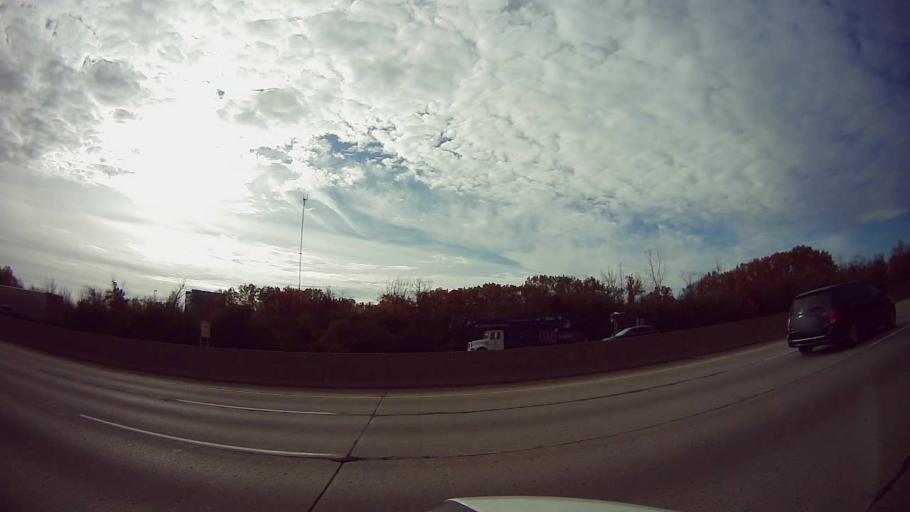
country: US
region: Michigan
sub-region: Oakland County
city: Franklin
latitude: 42.4909
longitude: -83.3130
